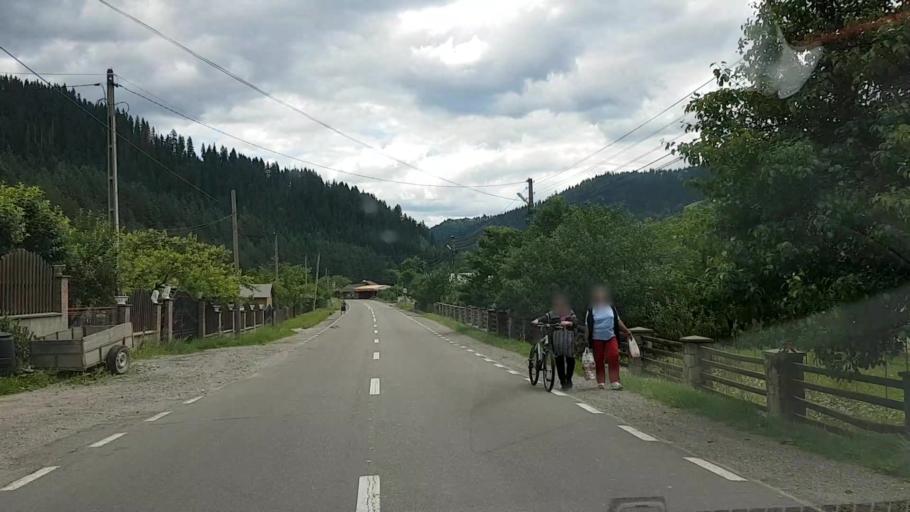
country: RO
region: Neamt
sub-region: Comuna Poiana Teiului
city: Poiana Teiului
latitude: 47.1294
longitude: 25.9018
